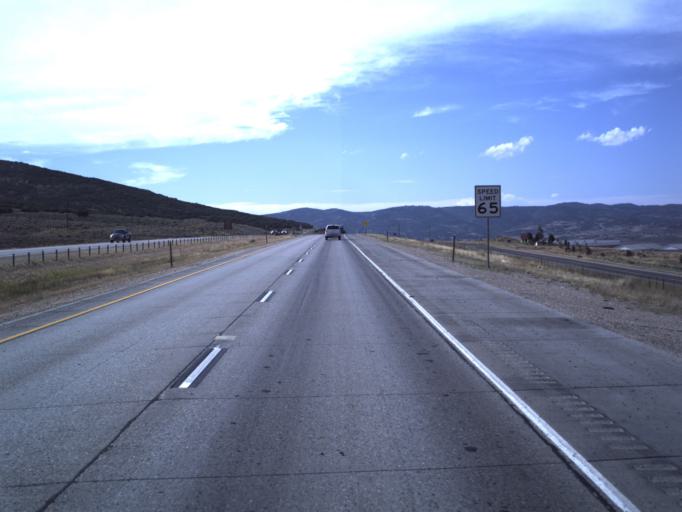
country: US
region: Utah
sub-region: Summit County
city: Park City
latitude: 40.6911
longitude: -111.4674
